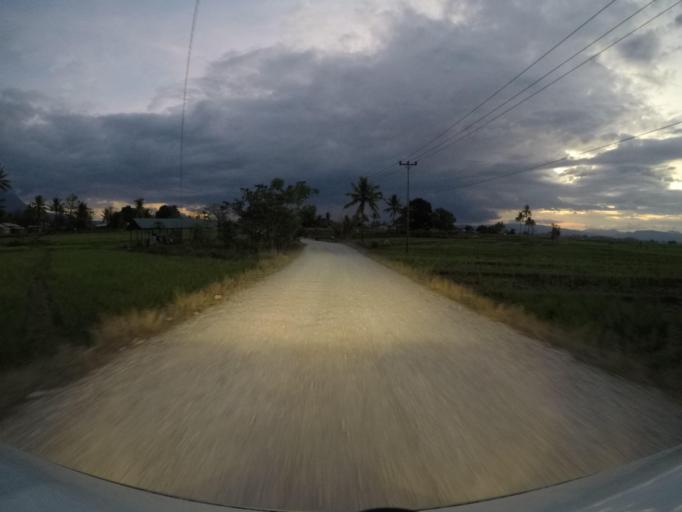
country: TL
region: Bobonaro
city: Maliana
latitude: -8.9822
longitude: 125.2126
